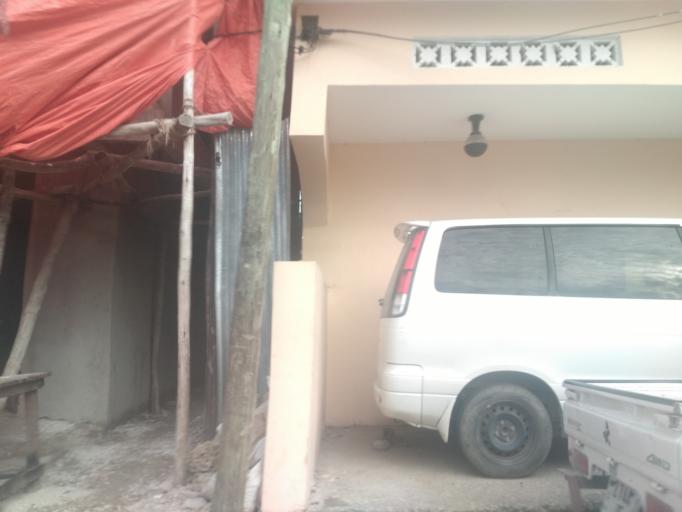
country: TZ
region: Zanzibar Urban/West
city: Zanzibar
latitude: -6.1591
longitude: 39.2018
